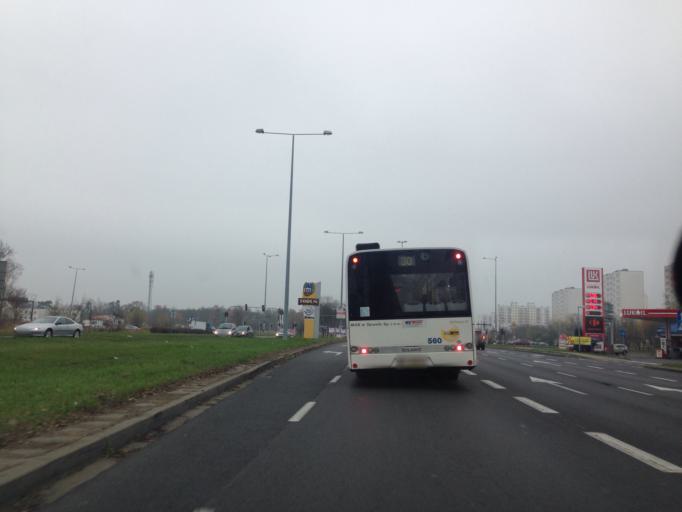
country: PL
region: Kujawsko-Pomorskie
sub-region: Powiat torunski
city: Lubicz Dolny
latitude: 53.0275
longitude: 18.6843
